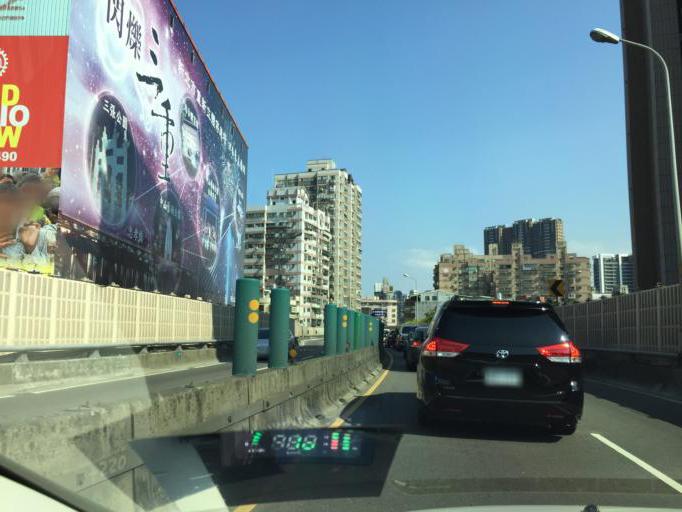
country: TW
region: Taipei
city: Taipei
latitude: 25.0585
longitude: 121.4893
